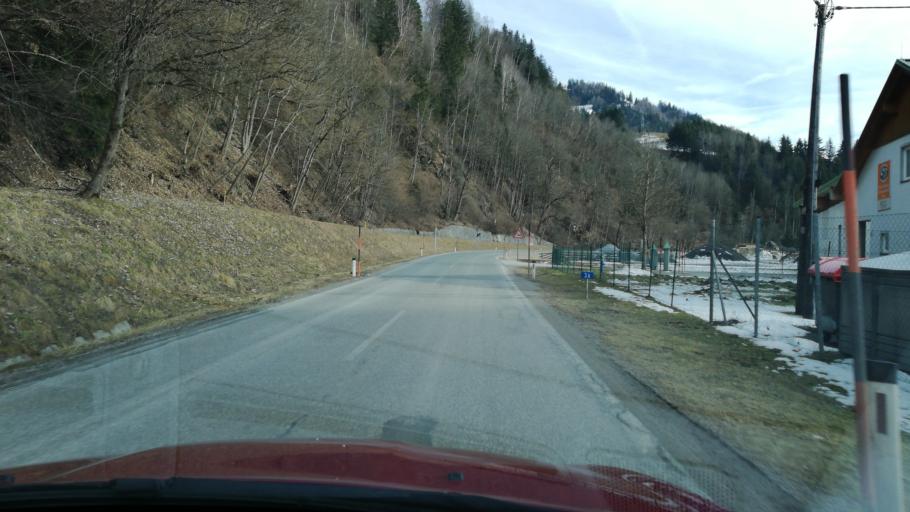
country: AT
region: Styria
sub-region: Politischer Bezirk Liezen
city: Irdning
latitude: 47.4970
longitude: 14.1033
